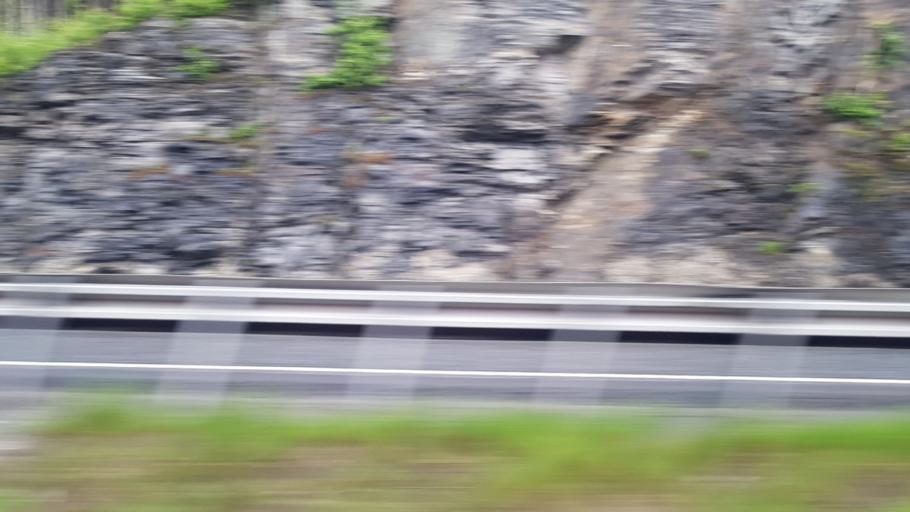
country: NO
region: Oppland
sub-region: Ringebu
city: Ringebu
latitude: 61.5363
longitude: 10.1116
